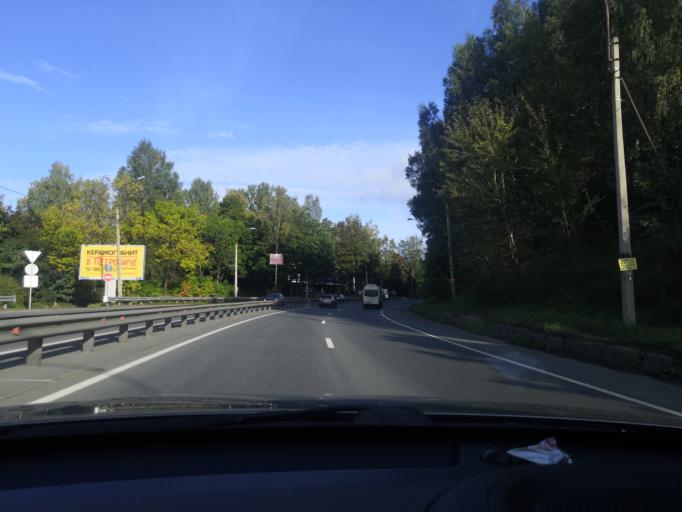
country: RU
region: St.-Petersburg
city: Pargolovo
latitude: 60.0801
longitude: 30.2645
